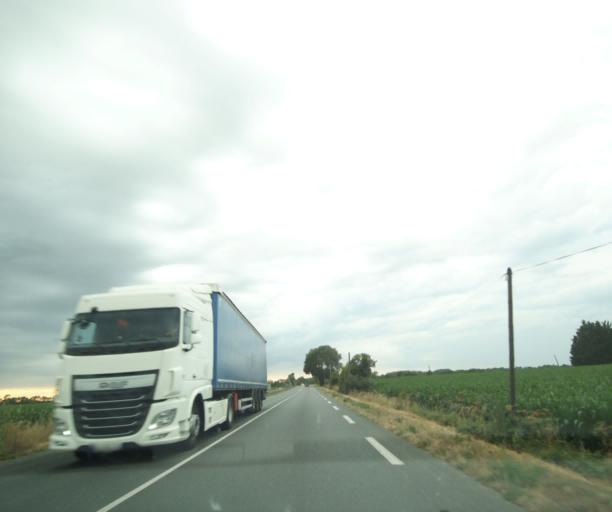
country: FR
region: Pays de la Loire
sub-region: Departement de la Vendee
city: Champagne-les-Marais
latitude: 46.4292
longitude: -1.0939
